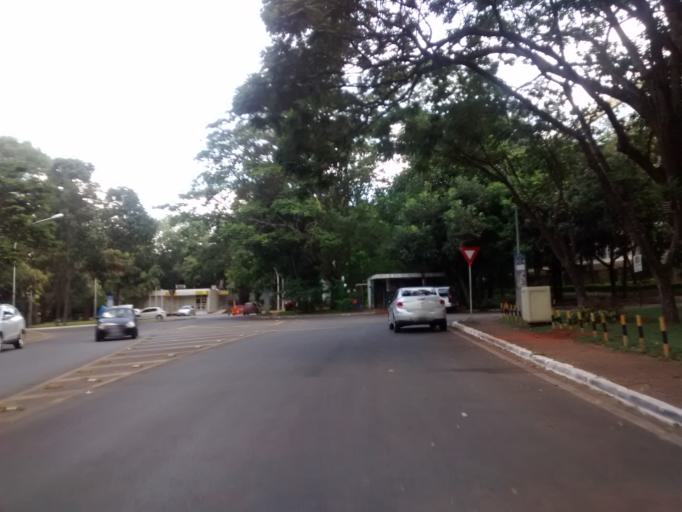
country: BR
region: Federal District
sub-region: Brasilia
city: Brasilia
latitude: -15.8065
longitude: -47.8945
